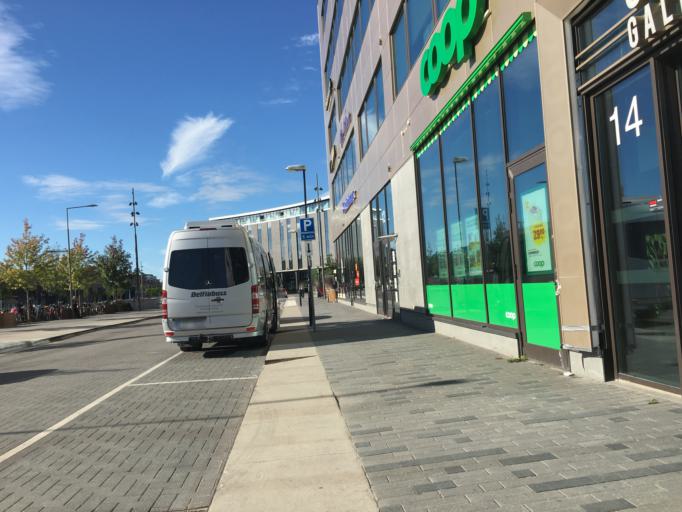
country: SE
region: Uppsala
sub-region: Uppsala Kommun
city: Uppsala
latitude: 59.8582
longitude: 17.6494
